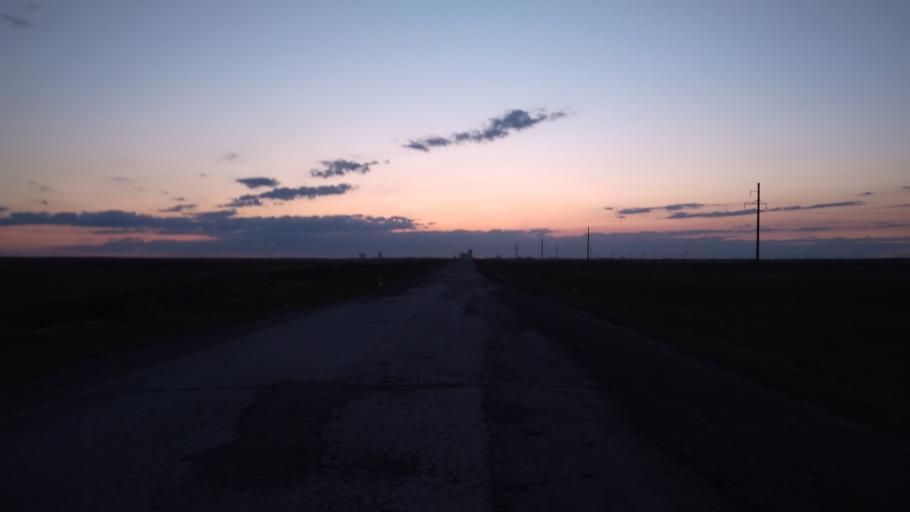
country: RU
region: Chelyabinsk
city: Troitsk
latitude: 54.0902
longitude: 61.6474
